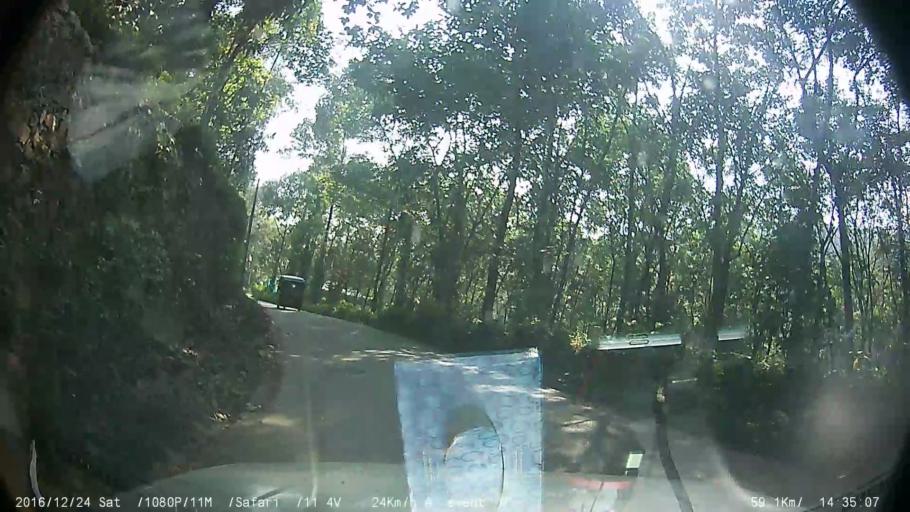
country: IN
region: Kerala
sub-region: Kottayam
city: Lalam
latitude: 9.8094
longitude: 76.7289
